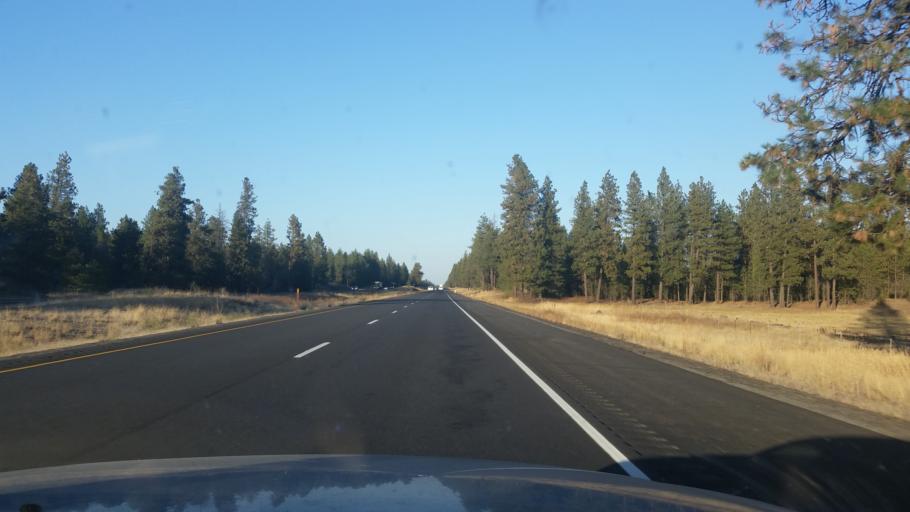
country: US
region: Washington
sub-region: Spokane County
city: Medical Lake
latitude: 47.4728
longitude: -117.7367
